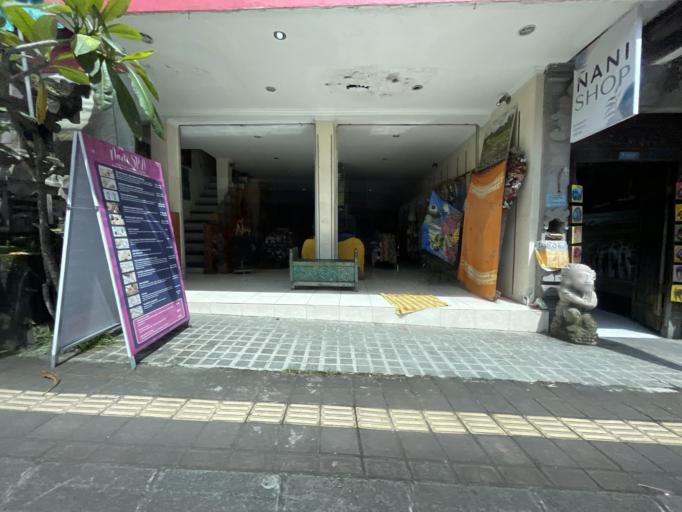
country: ID
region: Bali
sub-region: Kabupaten Gianyar
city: Ubud
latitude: -8.5137
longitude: 115.2607
